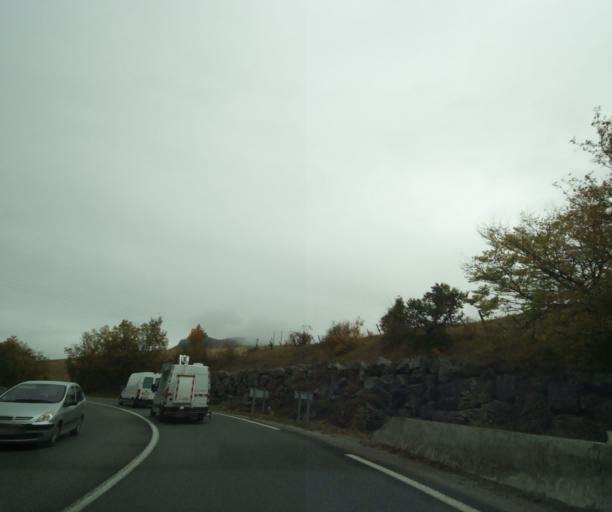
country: FR
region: Midi-Pyrenees
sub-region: Departement de l'Aveyron
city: Millau
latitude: 44.0866
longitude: 3.0878
